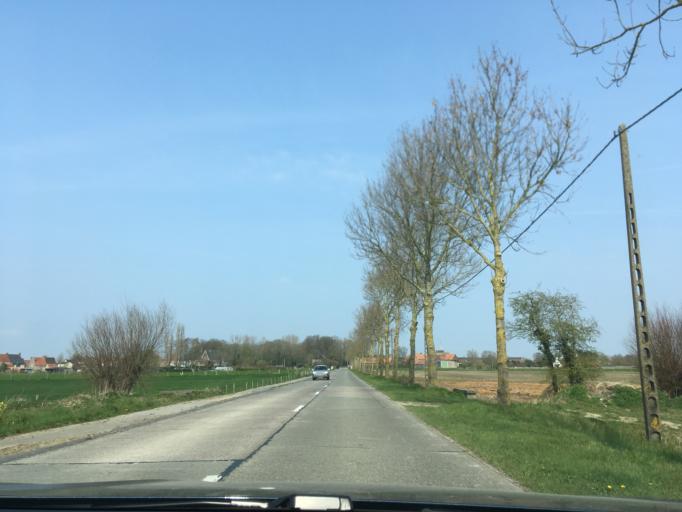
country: BE
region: Flanders
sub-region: Provincie West-Vlaanderen
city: Ardooie
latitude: 51.0292
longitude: 3.2096
